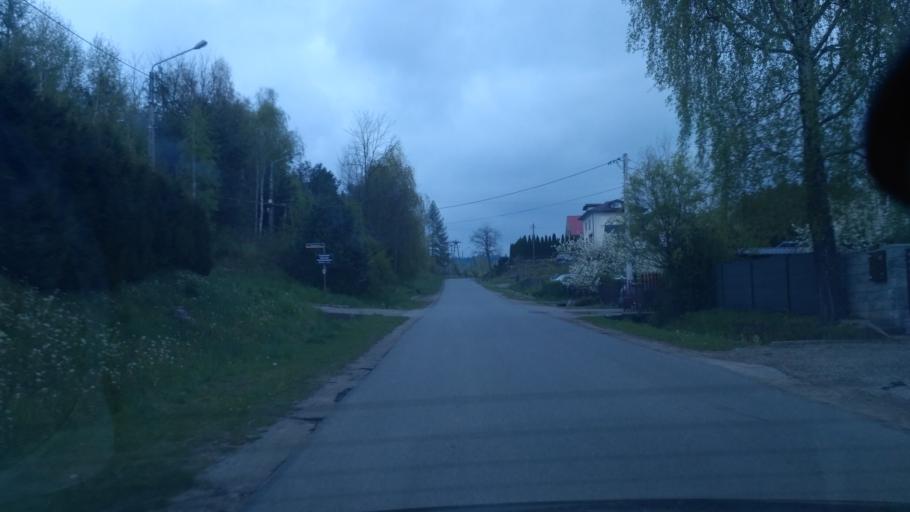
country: PL
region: Subcarpathian Voivodeship
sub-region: Powiat sanocki
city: Sanok
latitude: 49.5552
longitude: 22.2307
